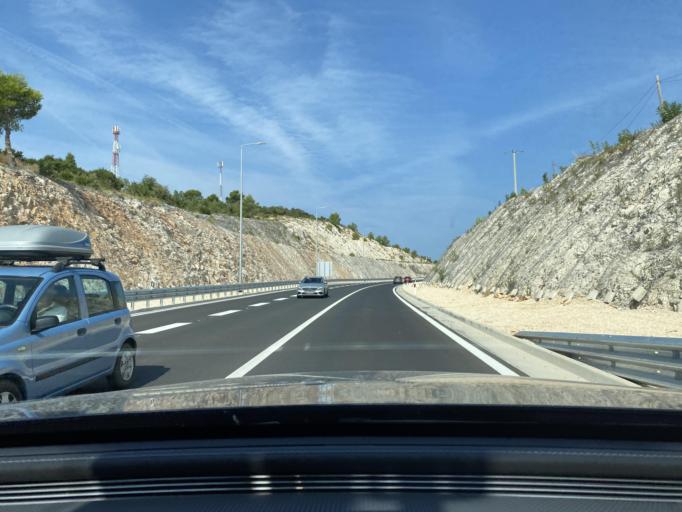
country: HR
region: Dubrovacko-Neretvanska
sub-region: Grad Dubrovnik
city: Opuzen
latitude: 42.9441
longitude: 17.5391
